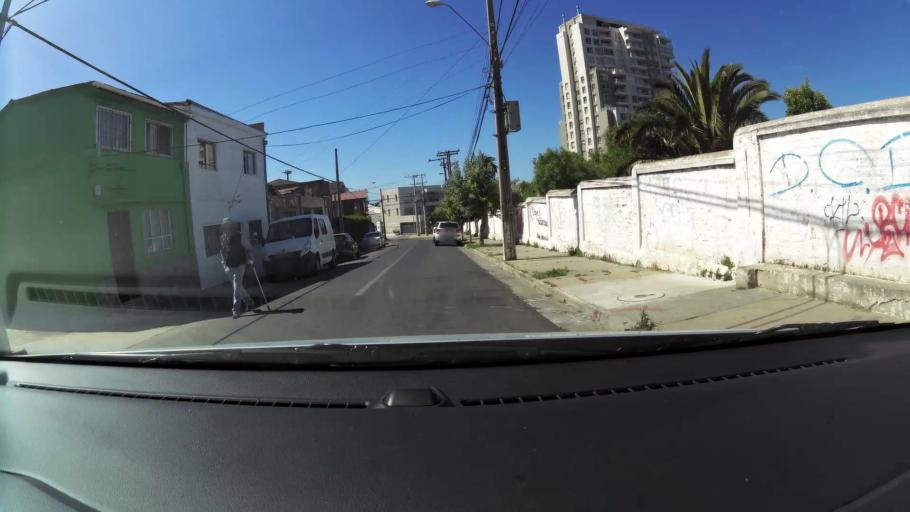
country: CL
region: Valparaiso
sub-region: Provincia de Valparaiso
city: Valparaiso
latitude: -33.0242
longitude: -71.6336
